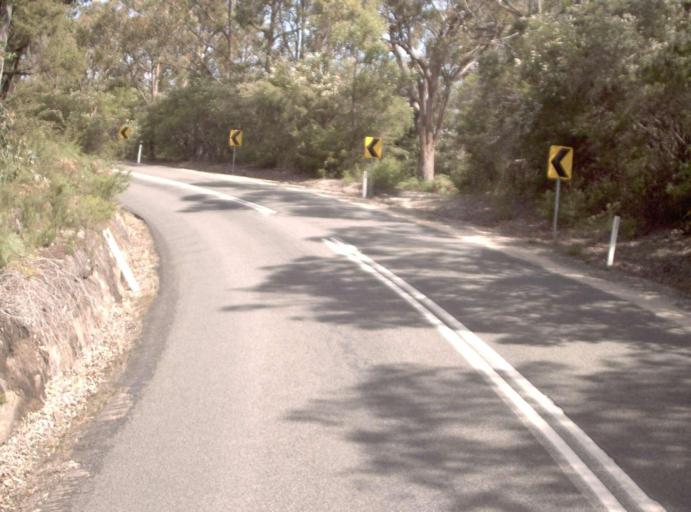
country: AU
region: New South Wales
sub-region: Bega Valley
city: Eden
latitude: -37.4947
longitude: 149.6620
